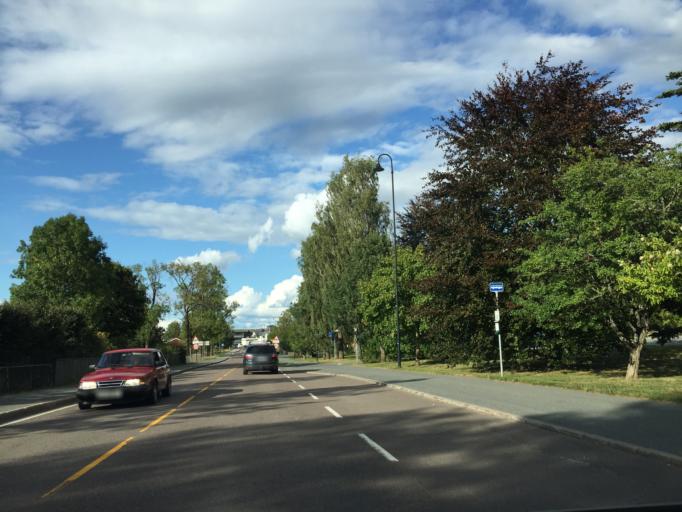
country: NO
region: Ostfold
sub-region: Trogstad
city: Skjonhaug
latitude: 59.6379
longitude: 11.3143
